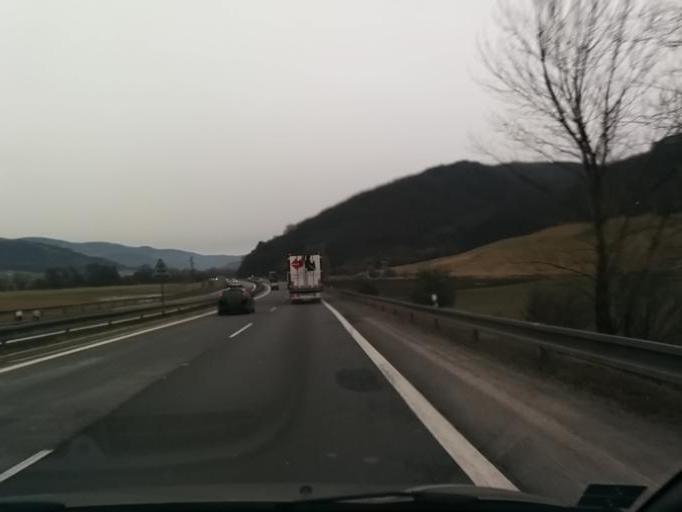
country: SK
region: Banskobystricky
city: Ziar nad Hronom
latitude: 48.5873
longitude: 18.9095
